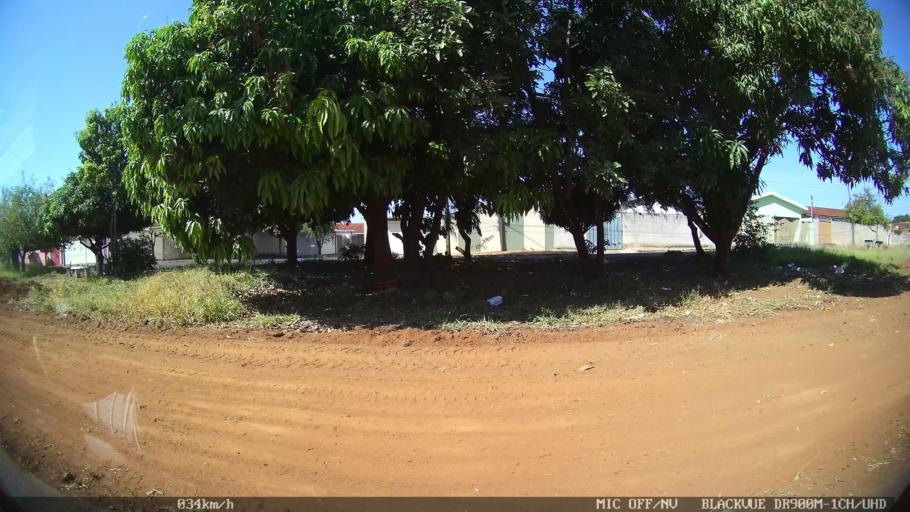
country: BR
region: Sao Paulo
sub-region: Batatais
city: Batatais
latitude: -20.8789
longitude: -47.5982
